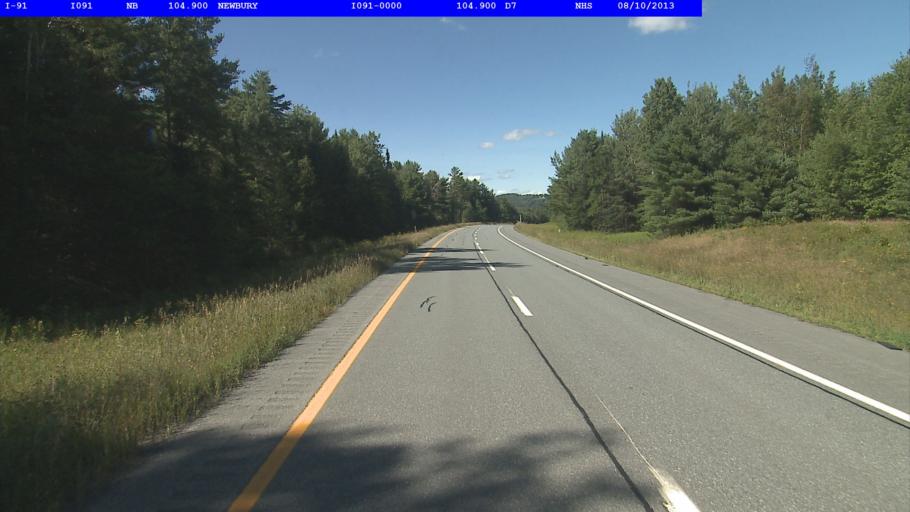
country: US
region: New Hampshire
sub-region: Grafton County
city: Haverhill
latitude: 44.0839
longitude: -72.1124
